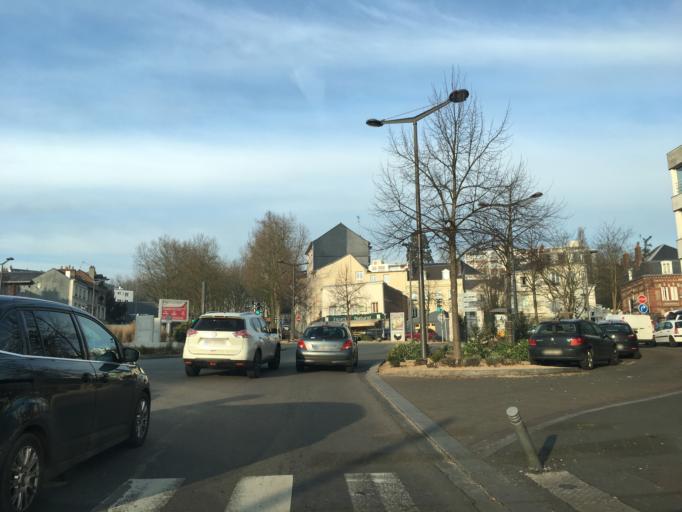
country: FR
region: Haute-Normandie
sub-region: Departement de la Seine-Maritime
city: Rouen
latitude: 49.4417
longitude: 1.1130
